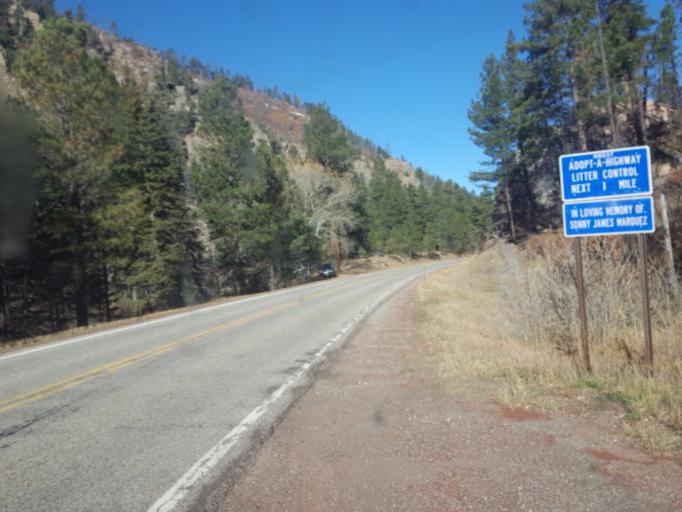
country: US
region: New Mexico
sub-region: Taos County
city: Ranchos de Taos
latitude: 36.1581
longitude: -105.5941
